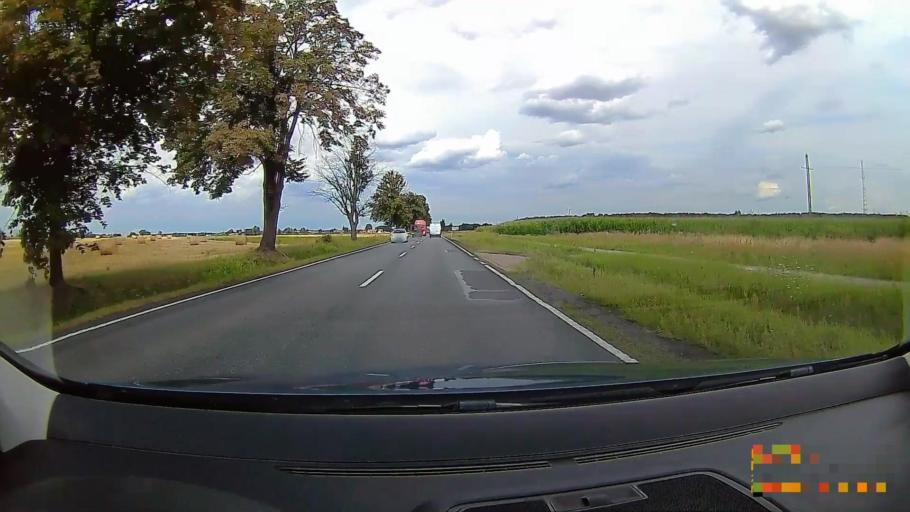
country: PL
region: Greater Poland Voivodeship
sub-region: Powiat koninski
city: Rychwal
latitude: 52.0842
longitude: 18.1625
